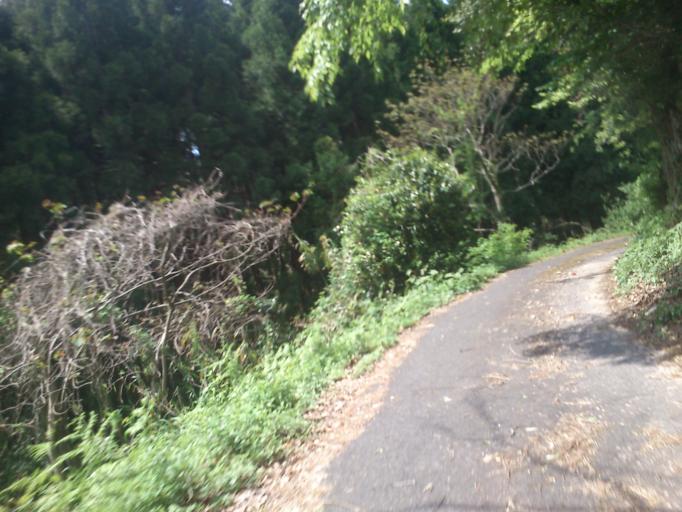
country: JP
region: Kyoto
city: Miyazu
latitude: 35.6992
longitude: 135.1316
